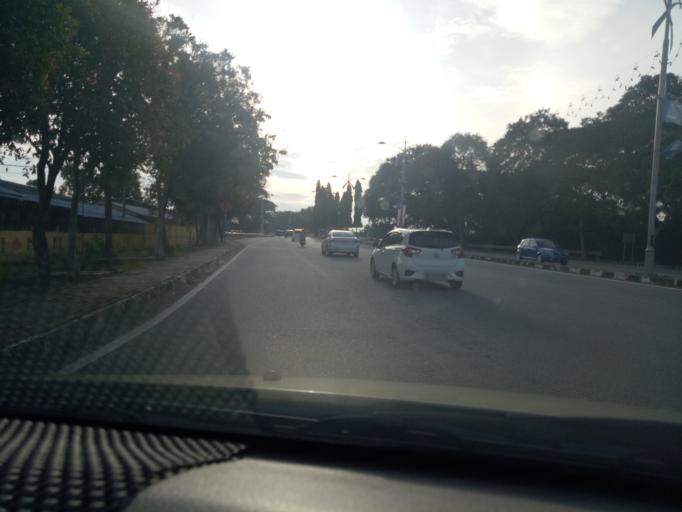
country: MY
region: Kedah
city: Alor Setar
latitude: 6.1436
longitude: 100.3700
